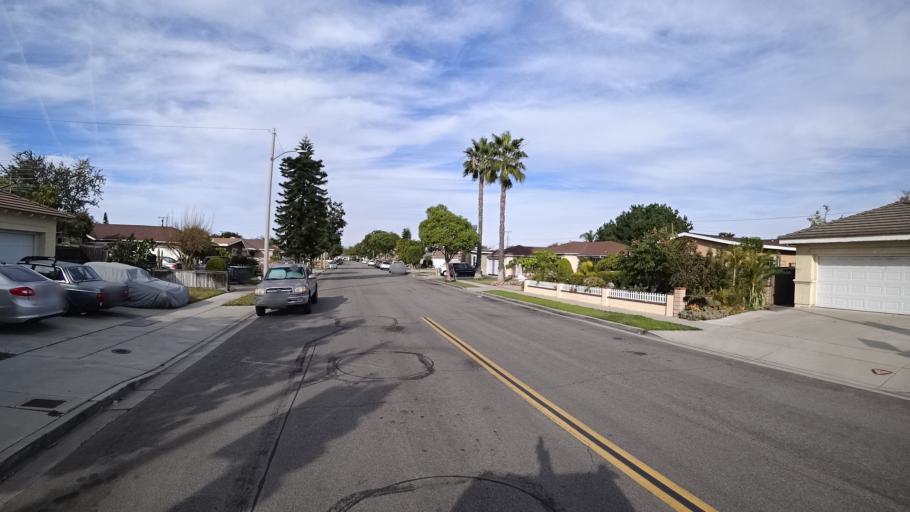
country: US
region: California
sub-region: Orange County
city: Garden Grove
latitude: 33.7672
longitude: -117.9351
